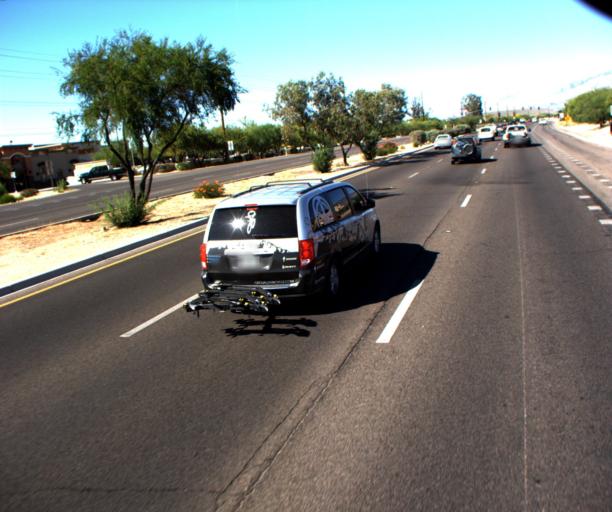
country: US
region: Arizona
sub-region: Pima County
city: Oro Valley
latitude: 32.4009
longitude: -110.9542
